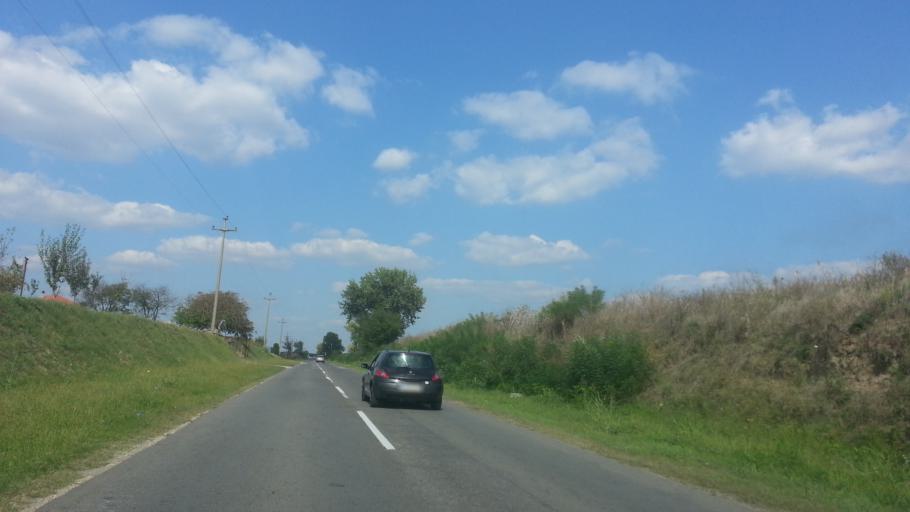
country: RS
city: Novi Banovci
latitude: 44.9324
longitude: 20.2801
